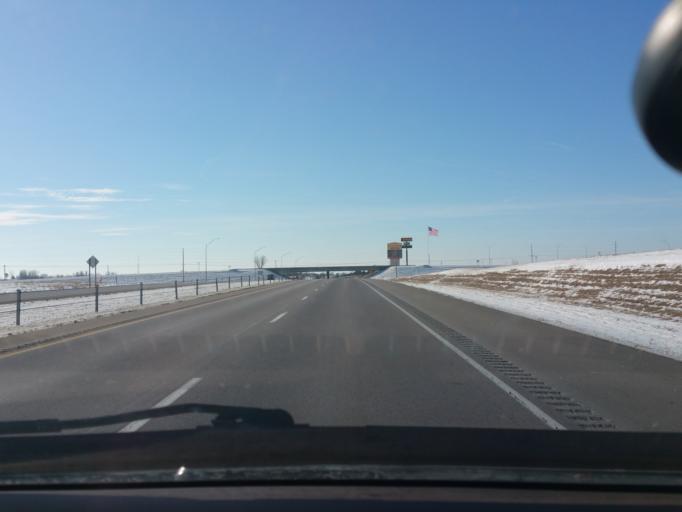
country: US
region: Iowa
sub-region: Clarke County
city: Osceola
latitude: 41.0451
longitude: -93.7881
